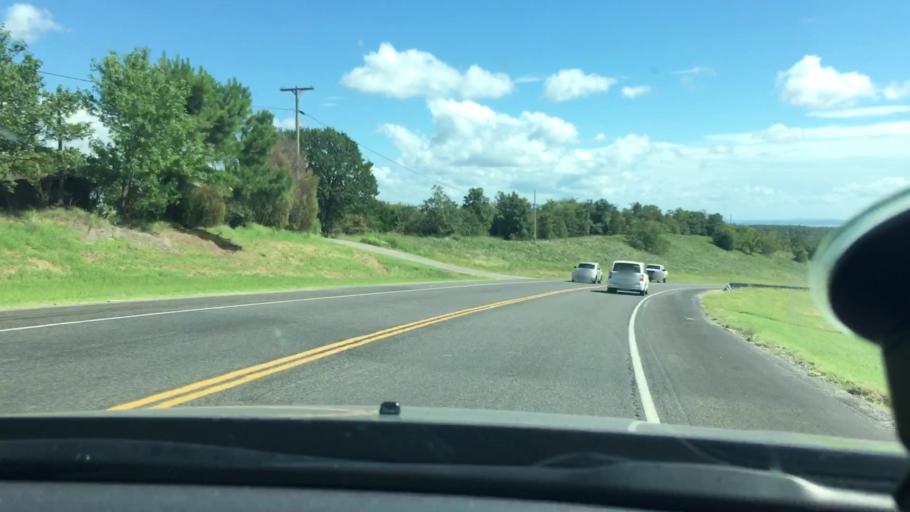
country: US
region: Oklahoma
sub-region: Sequoyah County
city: Vian
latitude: 35.5503
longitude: -94.9703
